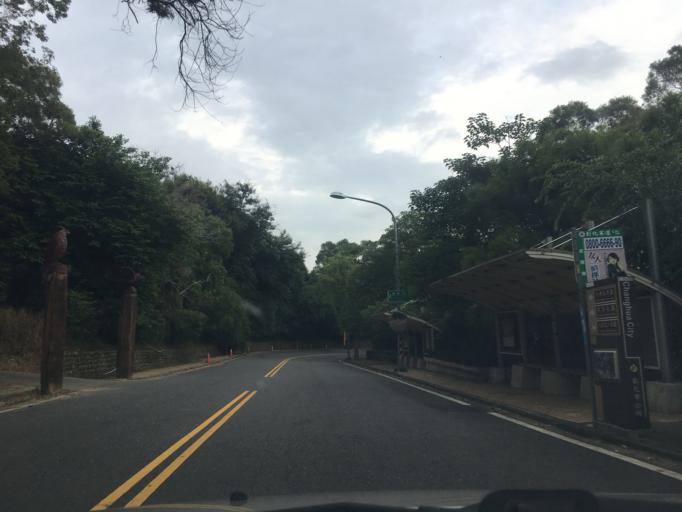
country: TW
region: Taiwan
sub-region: Changhua
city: Chang-hua
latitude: 24.0625
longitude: 120.5717
